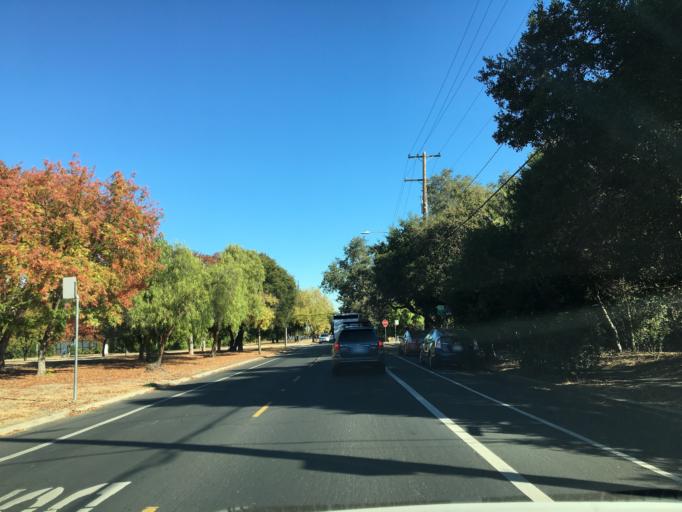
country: US
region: California
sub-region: Santa Clara County
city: Stanford
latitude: 37.4183
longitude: -122.1570
